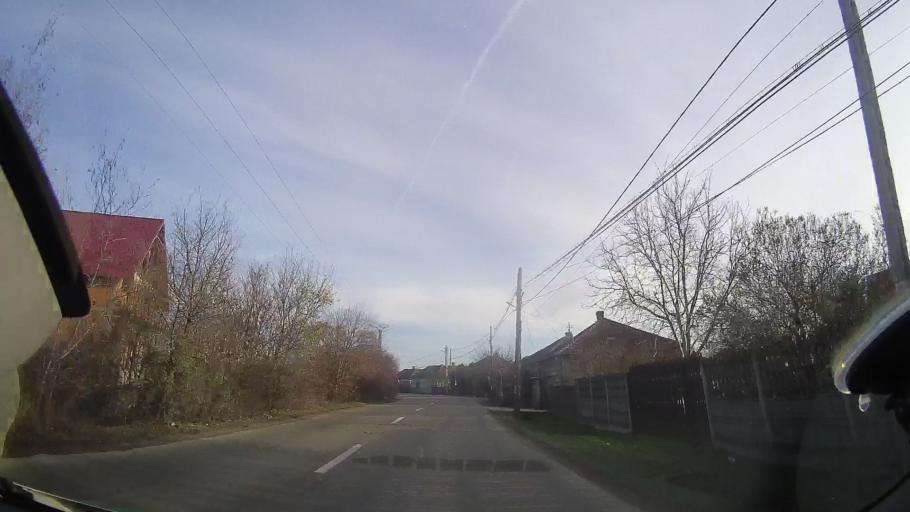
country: RO
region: Bihor
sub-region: Comuna Tileagd
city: Tileagd
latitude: 47.0684
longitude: 22.2053
